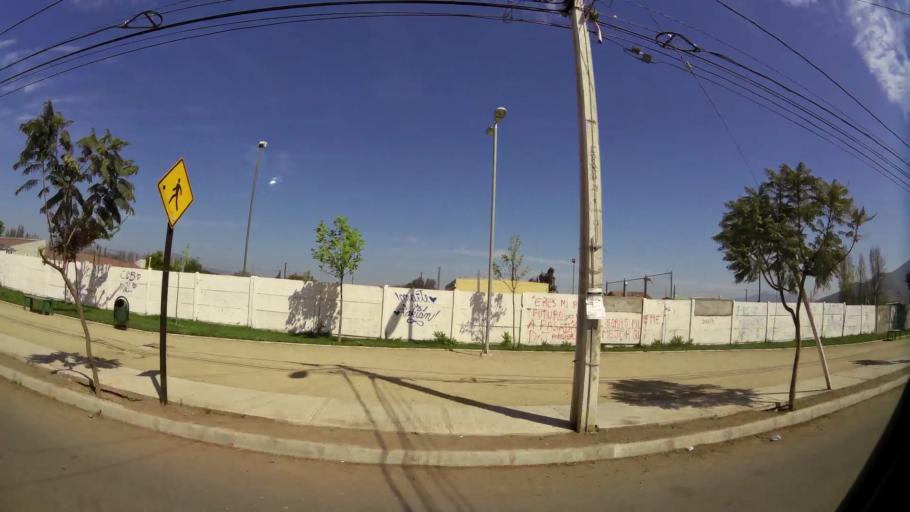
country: CL
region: Santiago Metropolitan
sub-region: Provincia de Talagante
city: Talagante
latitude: -33.6672
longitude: -70.9187
